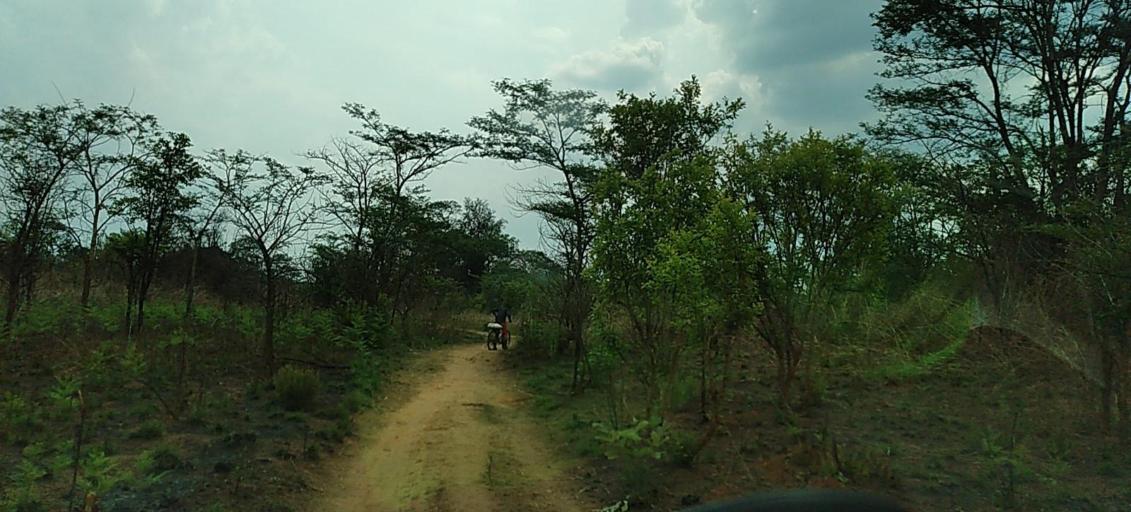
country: ZM
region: North-Western
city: Solwezi
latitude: -12.7950
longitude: 26.5310
